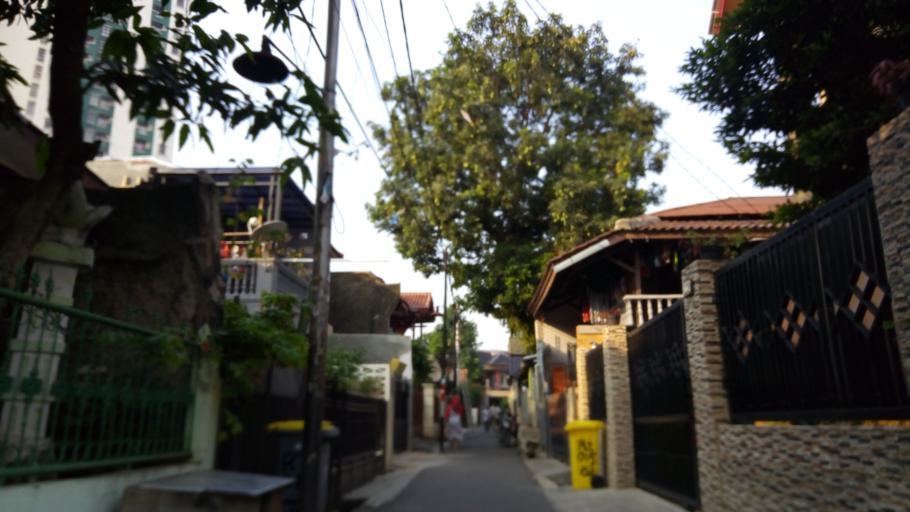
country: ID
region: Jakarta Raya
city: Jakarta
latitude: -6.1967
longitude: 106.8553
